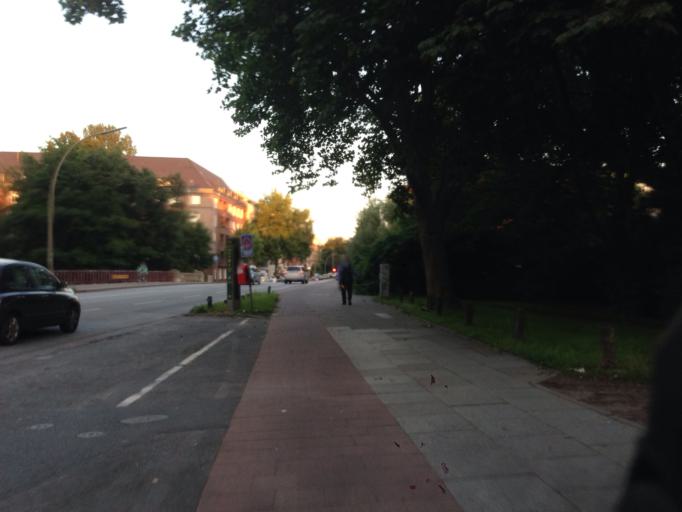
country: DE
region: Hamburg
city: Hamburg
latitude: 53.5881
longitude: 10.0163
